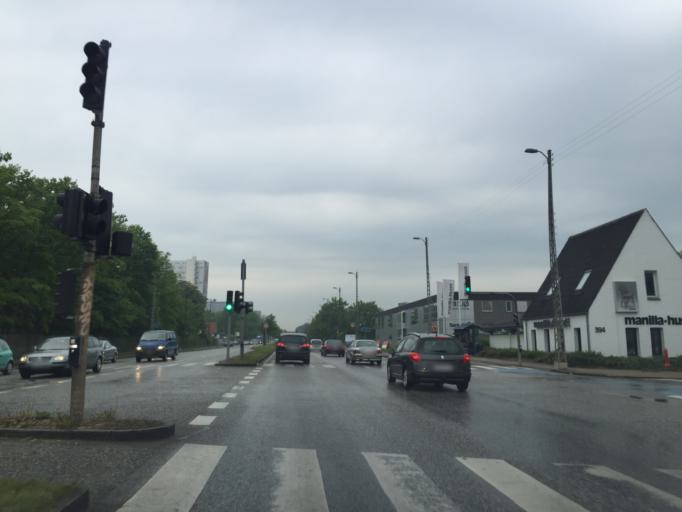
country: DK
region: Capital Region
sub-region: Rodovre Kommune
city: Rodovre
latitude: 55.6702
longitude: 12.4458
